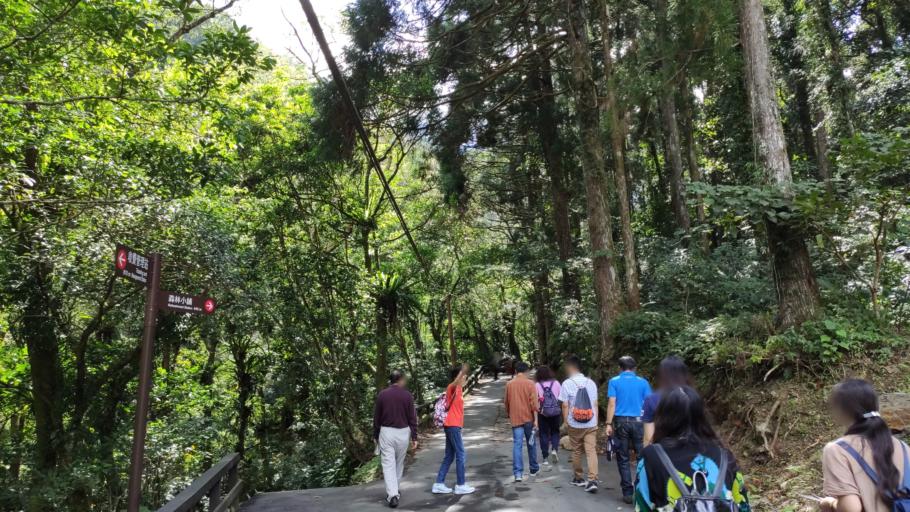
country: TW
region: Taiwan
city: Daxi
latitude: 24.8254
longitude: 121.4488
